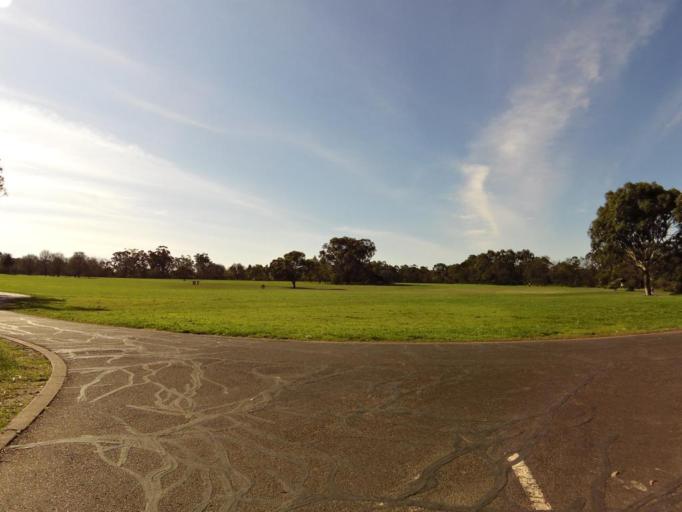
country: AU
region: Victoria
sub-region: Monash
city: Mulgrave
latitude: -37.8991
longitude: 145.2003
